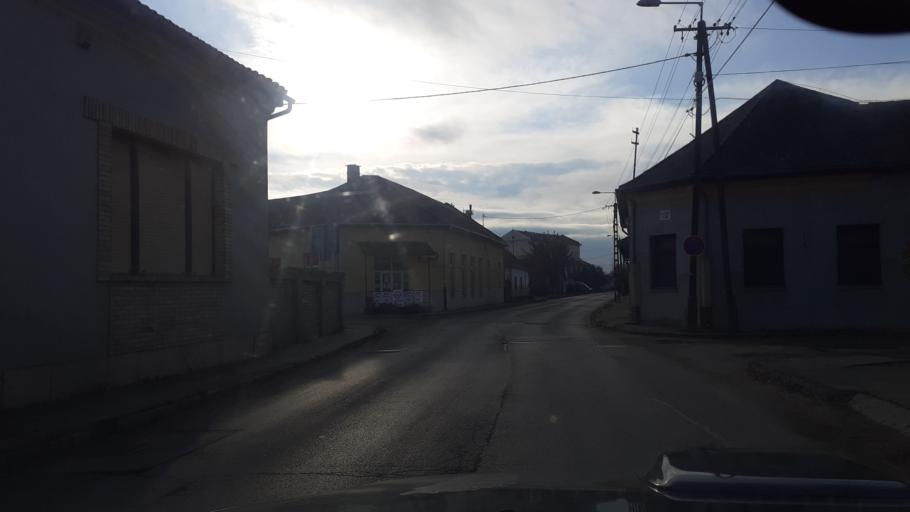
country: HU
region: Bacs-Kiskun
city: Kunszentmiklos
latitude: 47.0229
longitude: 19.1207
